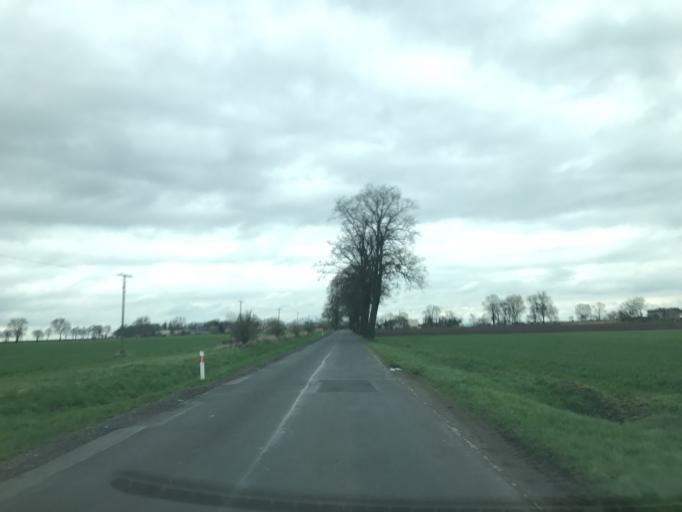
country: PL
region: Kujawsko-Pomorskie
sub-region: Powiat torunski
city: Lubianka
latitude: 53.1873
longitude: 18.4890
